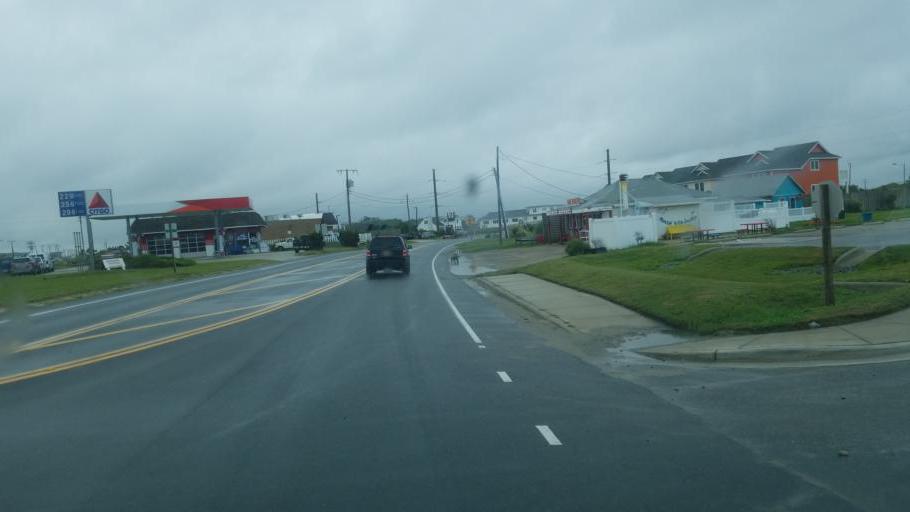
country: US
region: North Carolina
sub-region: Dare County
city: Nags Head
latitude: 35.9091
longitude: -75.5973
